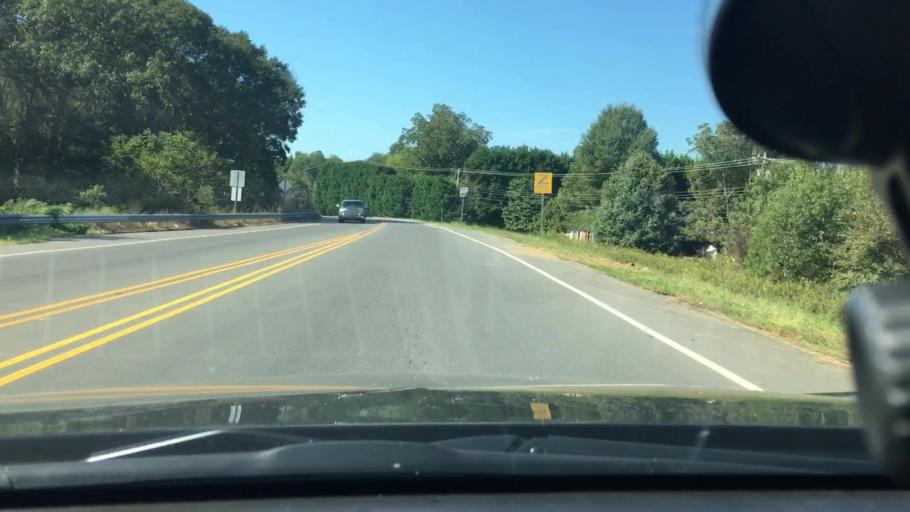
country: US
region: North Carolina
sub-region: Gaston County
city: Mount Holly
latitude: 35.2738
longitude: -80.9701
